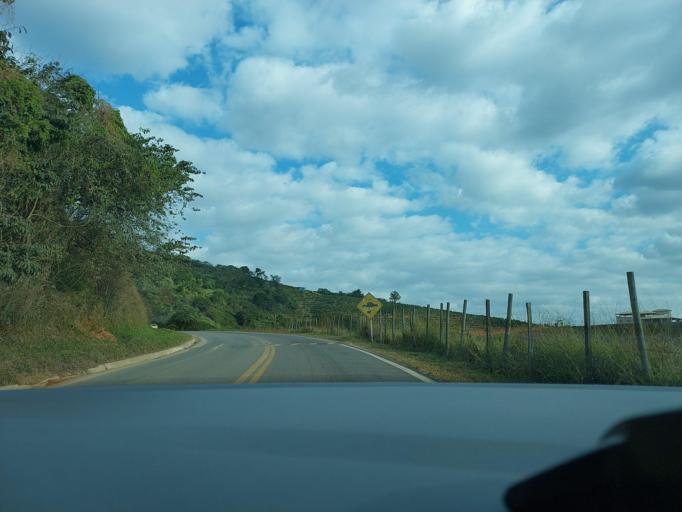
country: BR
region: Minas Gerais
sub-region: Visconde Do Rio Branco
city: Visconde do Rio Branco
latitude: -20.8998
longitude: -42.6538
